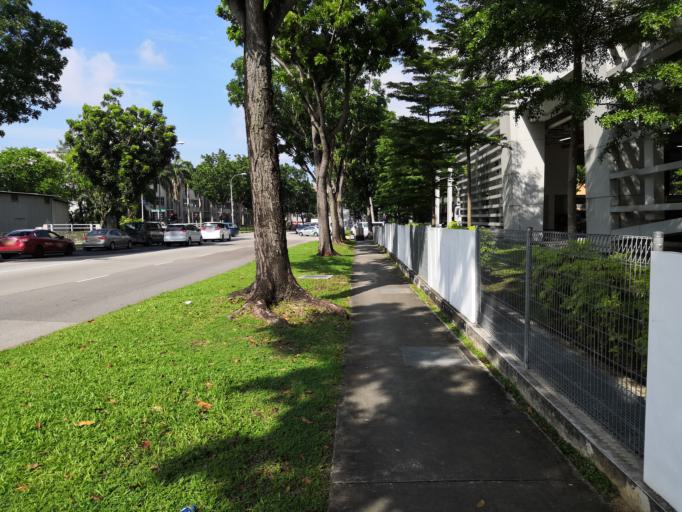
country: SG
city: Singapore
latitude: 1.3365
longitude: 103.9008
